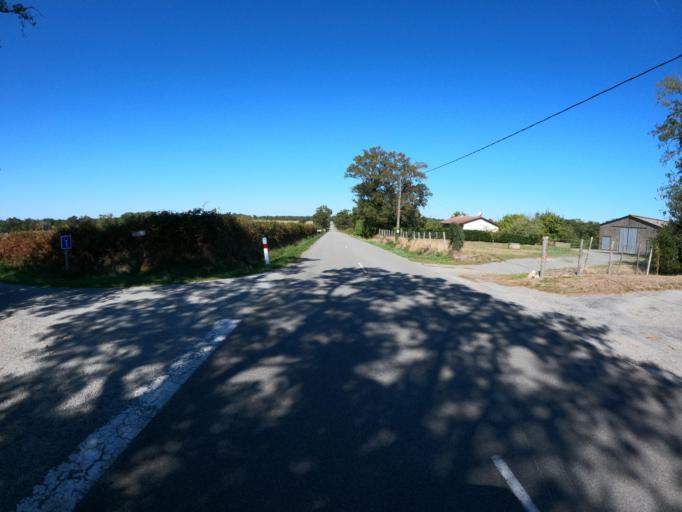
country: FR
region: Limousin
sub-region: Departement de la Haute-Vienne
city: Le Dorat
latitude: 46.2699
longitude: 1.0254
